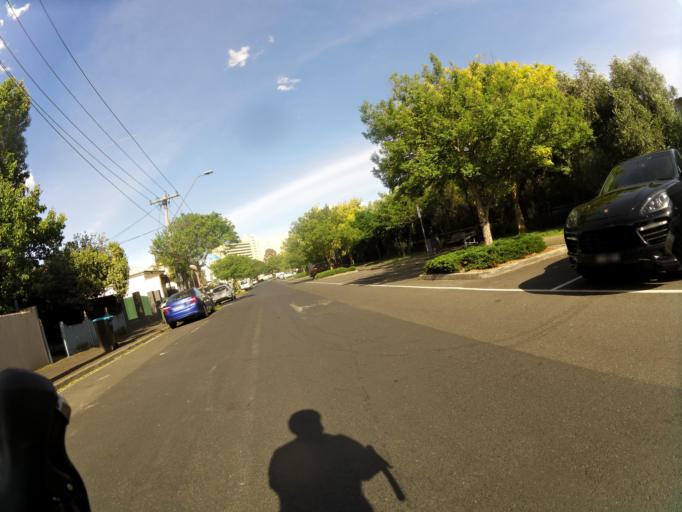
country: AU
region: Victoria
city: Windsor
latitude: -37.8450
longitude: 144.9920
